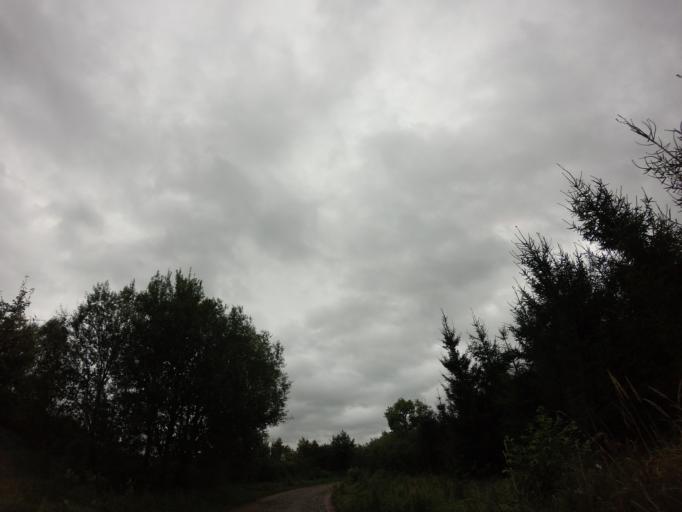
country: PL
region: West Pomeranian Voivodeship
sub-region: Powiat choszczenski
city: Choszczno
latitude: 53.1880
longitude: 15.3413
